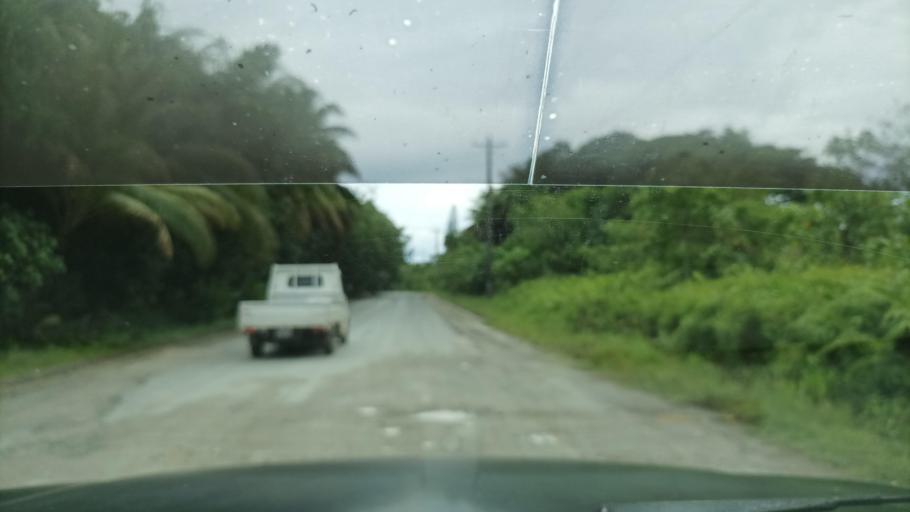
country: FM
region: Yap
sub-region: Weloy Municipality
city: Colonia
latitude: 9.5471
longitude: 138.1481
